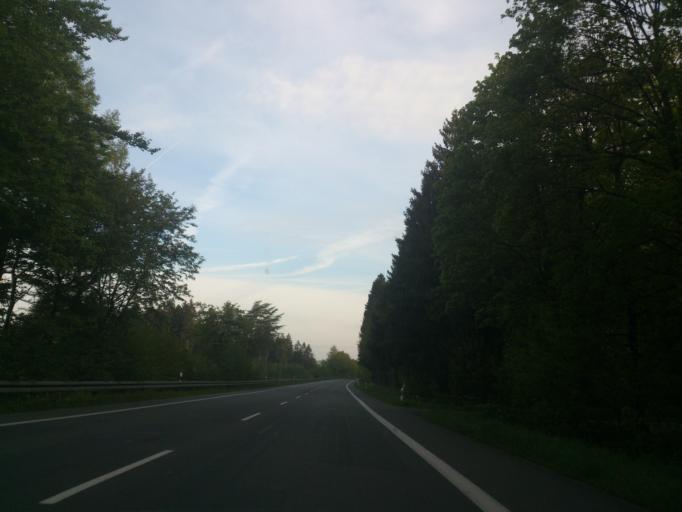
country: DE
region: North Rhine-Westphalia
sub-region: Regierungsbezirk Detmold
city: Bad Driburg
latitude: 51.6943
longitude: 8.9596
